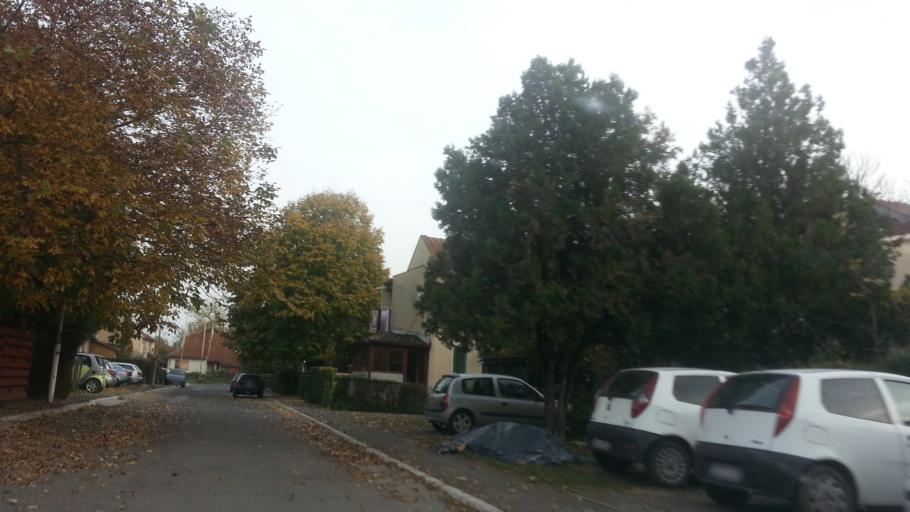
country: RS
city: Novi Banovci
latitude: 44.8952
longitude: 20.2843
